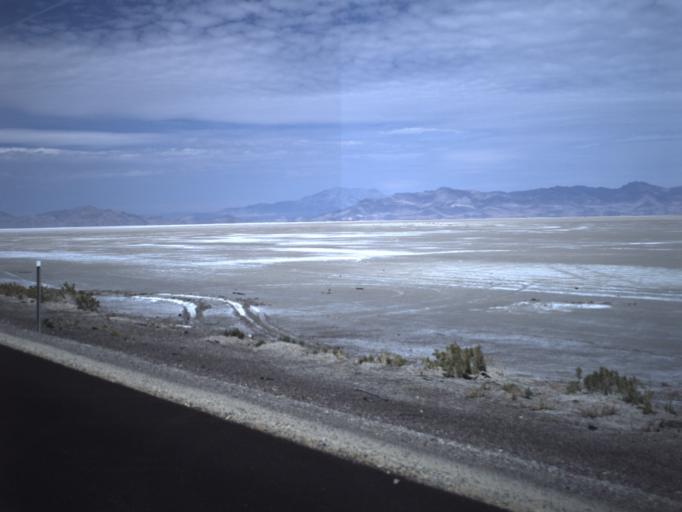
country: US
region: Utah
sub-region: Tooele County
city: Wendover
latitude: 40.7342
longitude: -113.6022
